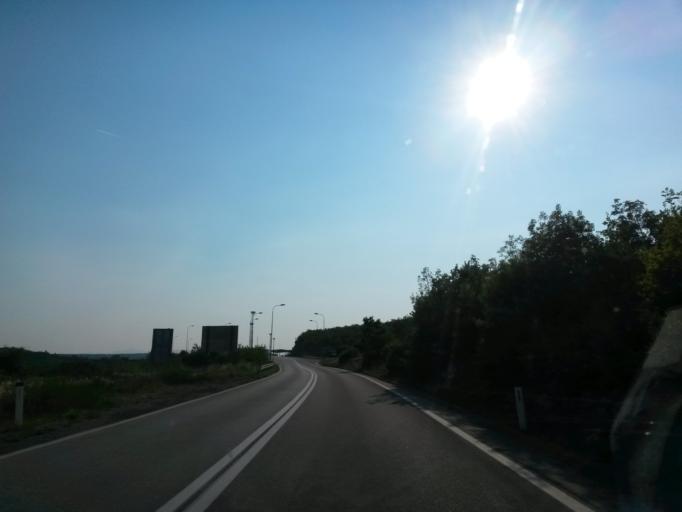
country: BA
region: Federation of Bosnia and Herzegovina
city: Podhum
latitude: 43.6123
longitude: 16.9820
